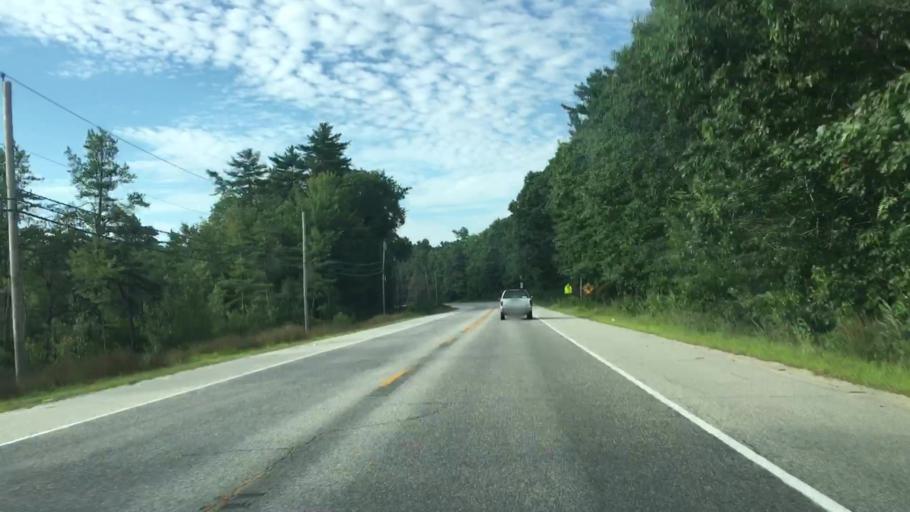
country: US
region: Maine
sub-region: Cumberland County
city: Raymond
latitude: 43.8670
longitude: -70.4658
